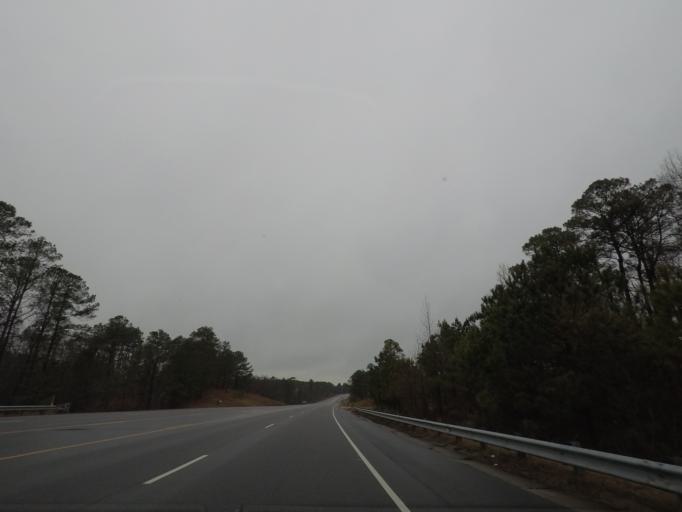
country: US
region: North Carolina
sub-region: Lee County
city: Broadway
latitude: 35.3456
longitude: -79.1064
